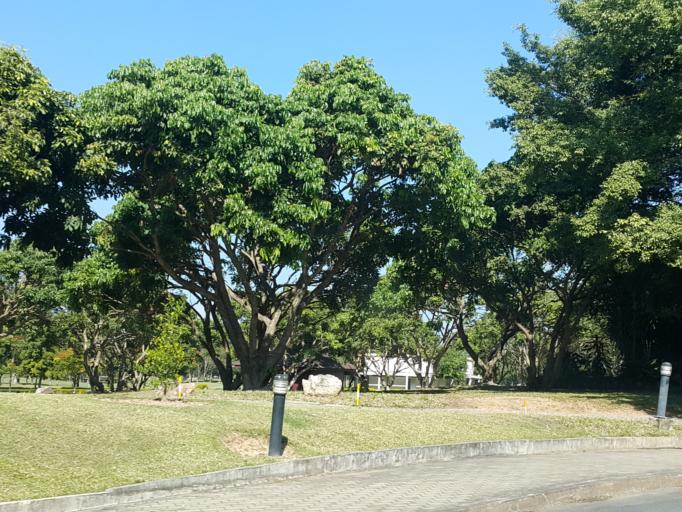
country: TH
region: Chiang Mai
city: Mae Taeng
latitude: 19.0257
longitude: 98.9884
